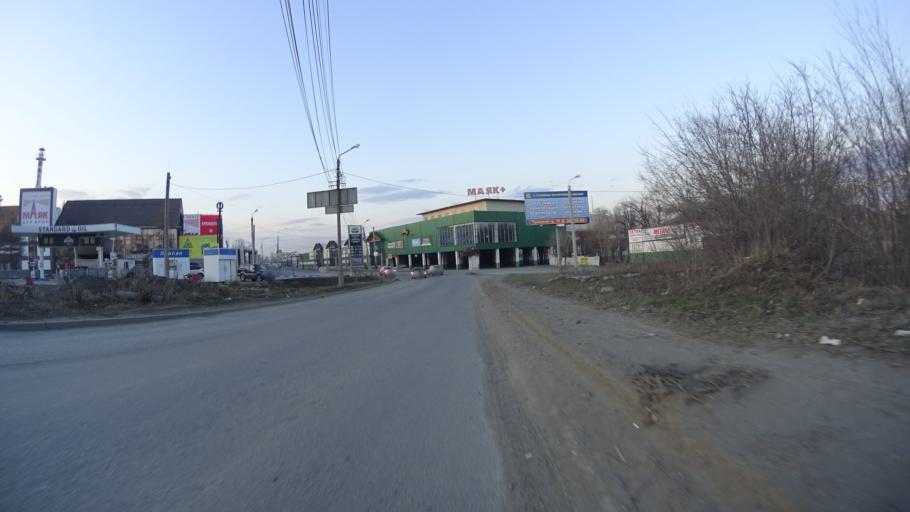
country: RU
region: Chelyabinsk
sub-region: Gorod Chelyabinsk
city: Chelyabinsk
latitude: 55.1179
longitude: 61.3858
